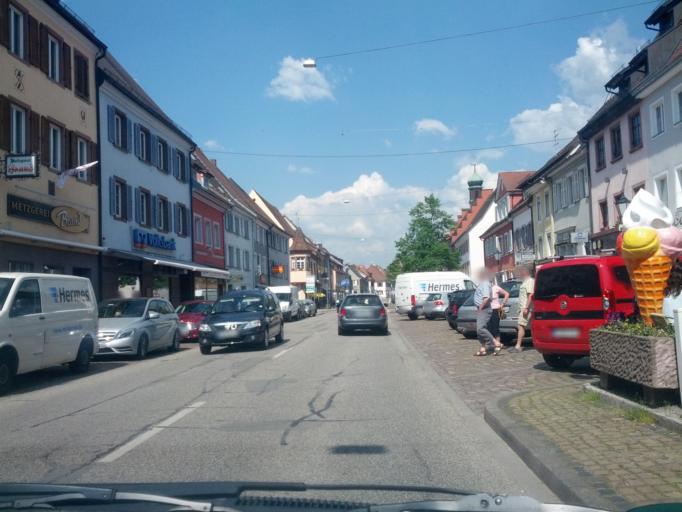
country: DE
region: Baden-Wuerttemberg
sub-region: Freiburg Region
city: Kenzingen
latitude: 48.1911
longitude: 7.7679
